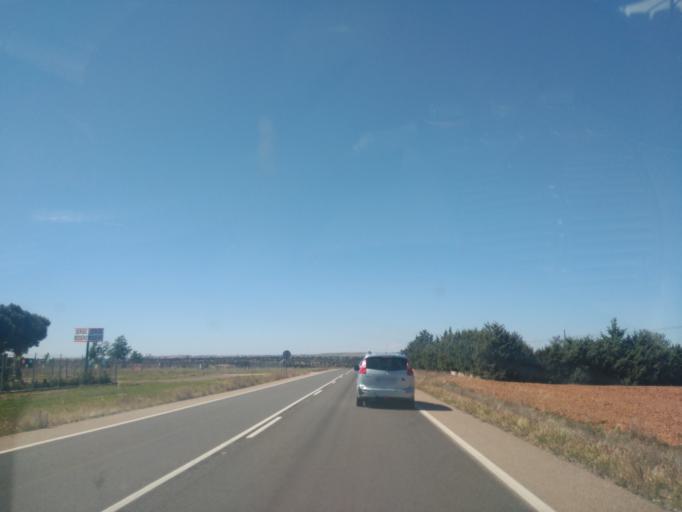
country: ES
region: Castille and Leon
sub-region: Provincia de Salamanca
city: Calvarrasa de Arriba
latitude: 40.9125
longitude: -5.5968
